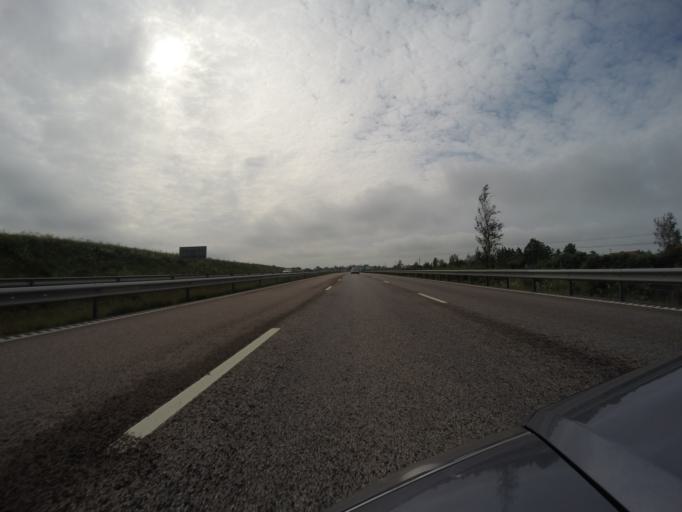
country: SE
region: Skane
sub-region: Helsingborg
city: Glumslov
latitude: 55.9477
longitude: 12.8104
